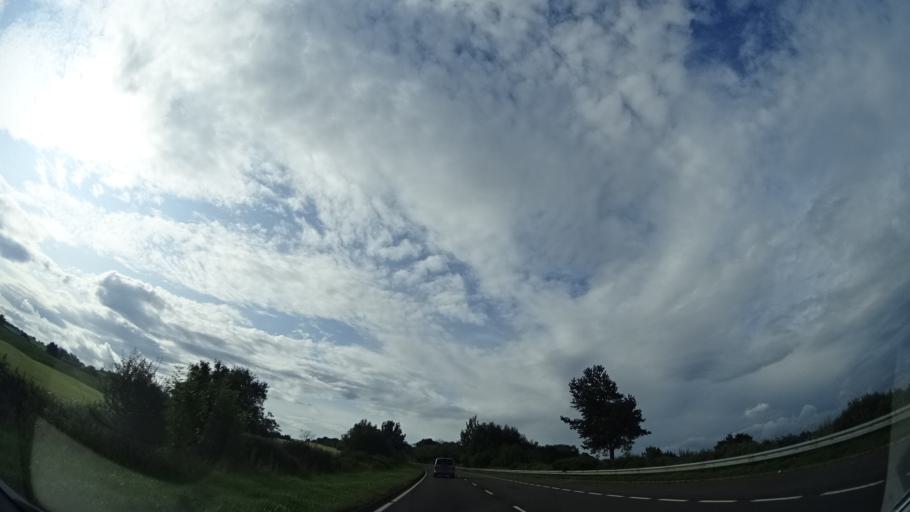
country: GB
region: Scotland
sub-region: Highland
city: Conon Bridge
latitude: 57.5595
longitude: -4.4189
